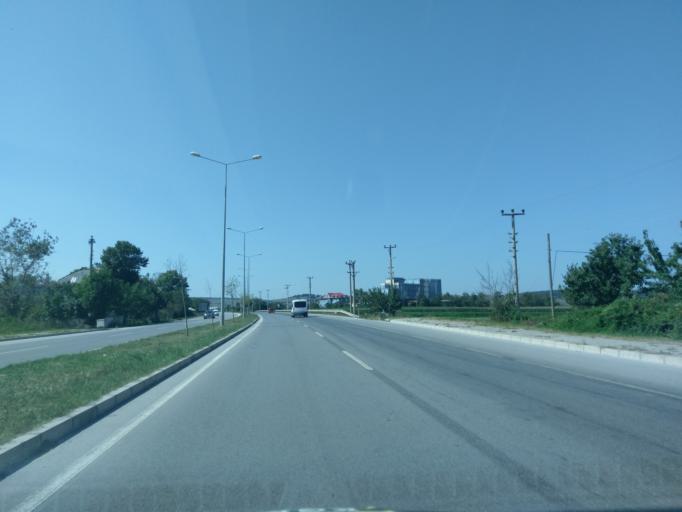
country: TR
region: Samsun
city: Bafra
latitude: 41.5714
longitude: 35.8722
